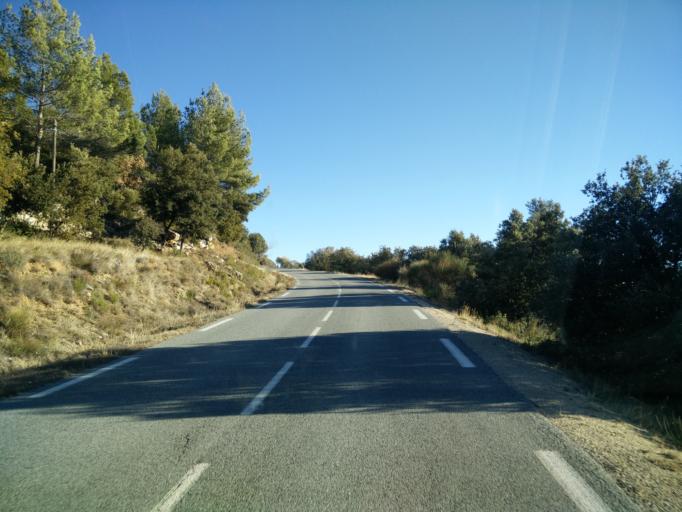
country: FR
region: Provence-Alpes-Cote d'Azur
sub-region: Departement du Var
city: Villecroze
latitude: 43.5932
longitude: 6.2905
